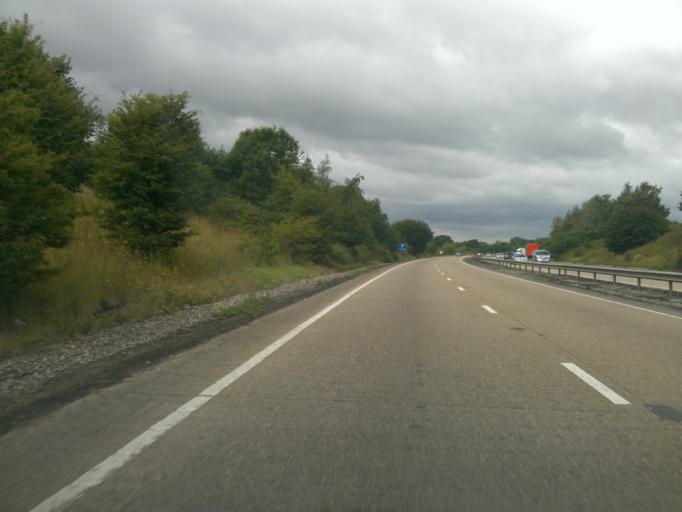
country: GB
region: England
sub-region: Essex
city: Alresford
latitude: 51.8863
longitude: 1.0225
